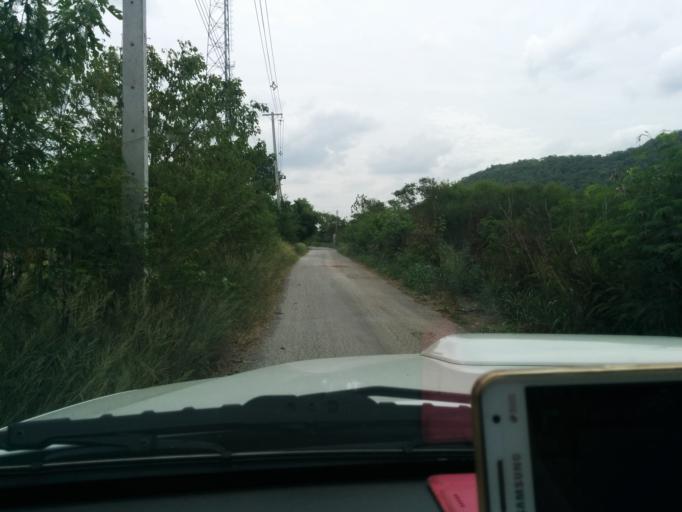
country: TH
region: Sara Buri
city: Muak Lek
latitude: 14.6168
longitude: 101.2084
